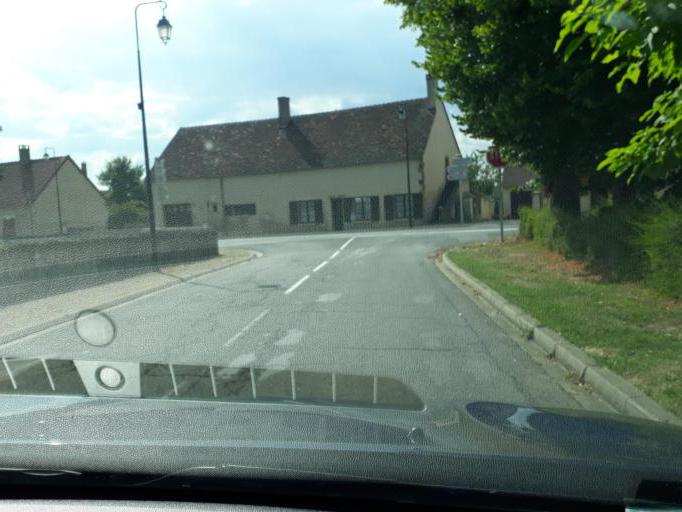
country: FR
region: Centre
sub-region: Departement du Cher
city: Nerondes
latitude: 47.0488
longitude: 2.8708
